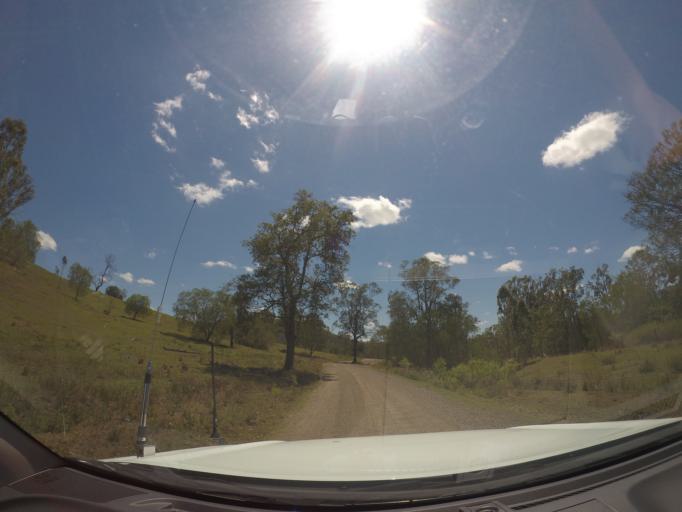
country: AU
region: Queensland
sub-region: Logan
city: Cedar Vale
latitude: -27.8639
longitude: 152.8534
